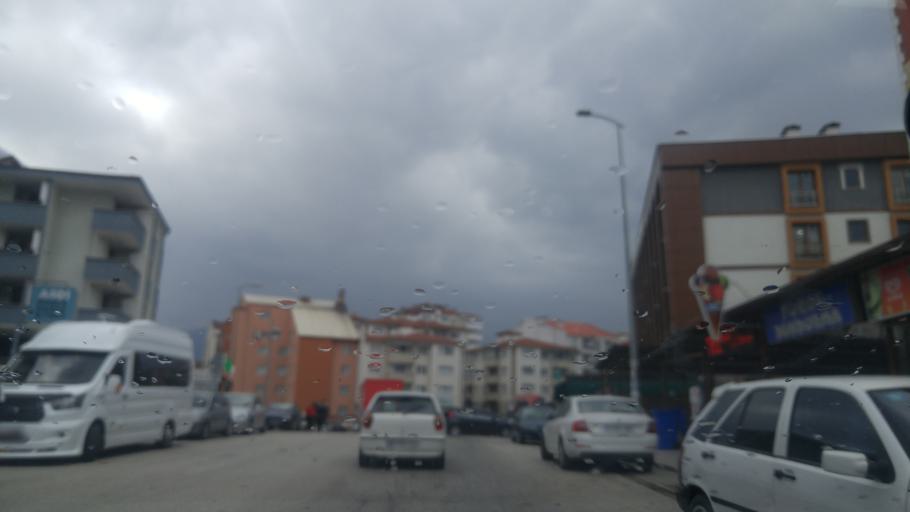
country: TR
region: Karabuk
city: Safranbolu
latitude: 41.2183
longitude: 32.6681
